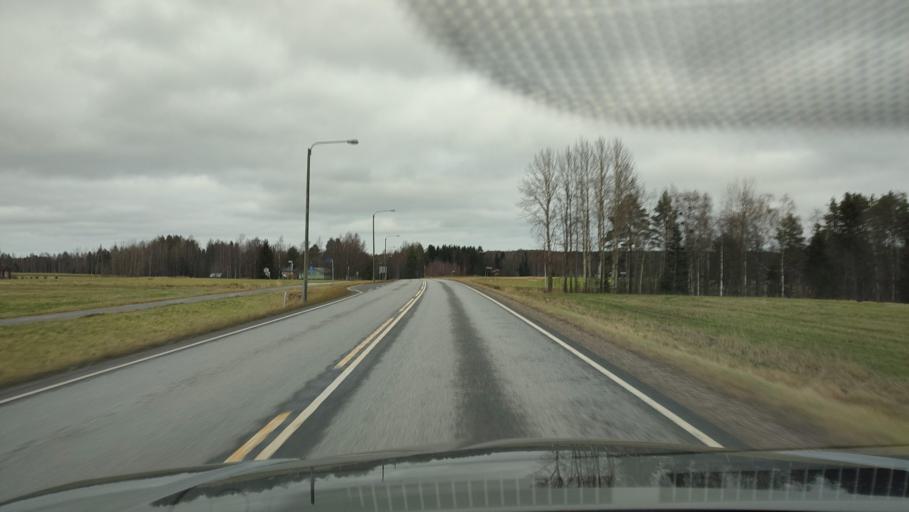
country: FI
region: Southern Ostrobothnia
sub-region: Seinaejoki
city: Kurikka
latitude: 62.5876
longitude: 22.4076
